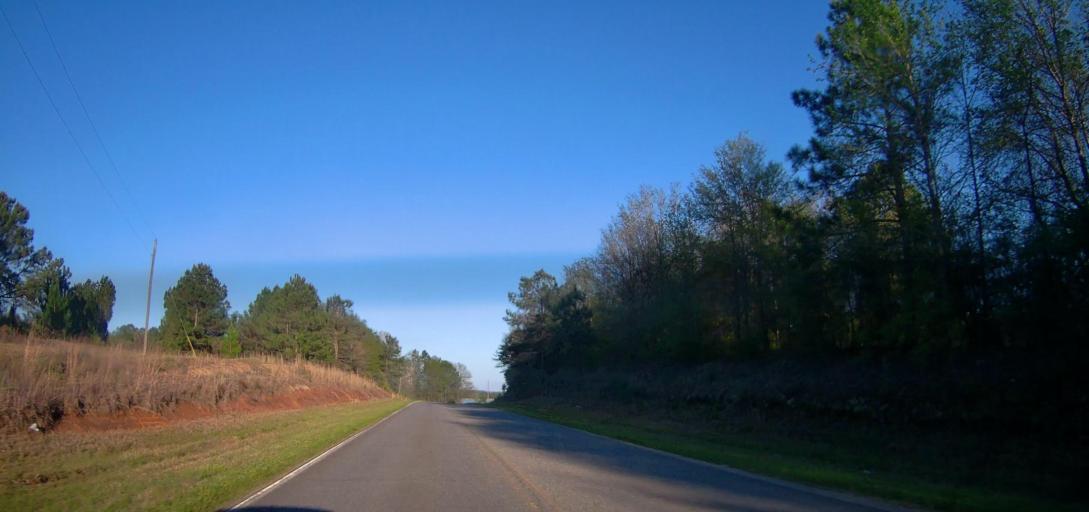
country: US
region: Georgia
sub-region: Wilkinson County
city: Irwinton
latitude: 32.8708
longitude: -83.2409
